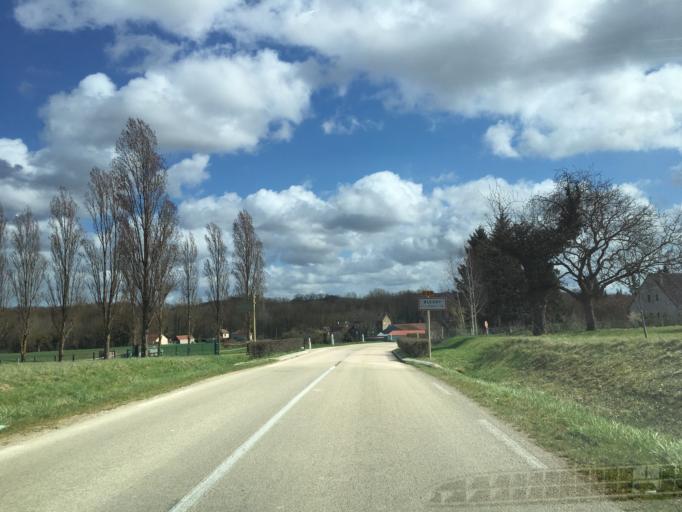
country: FR
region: Bourgogne
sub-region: Departement de l'Yonne
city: Aillant-sur-Tholon
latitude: 47.8448
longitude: 3.3907
